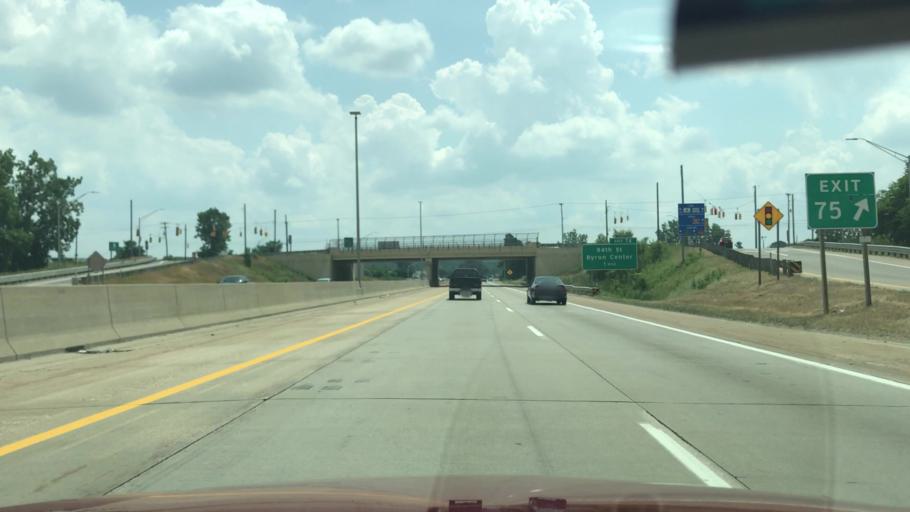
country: US
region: Michigan
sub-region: Kent County
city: Cutlerville
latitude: 42.8277
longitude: -85.6728
